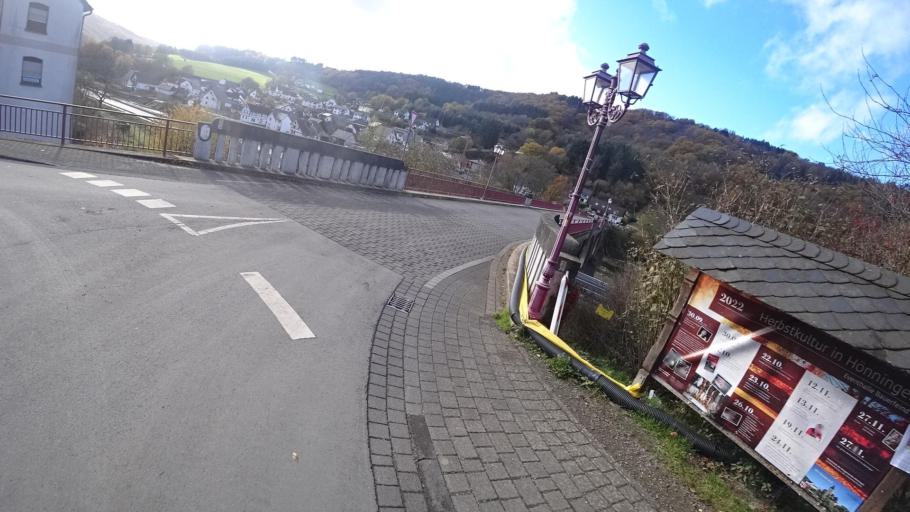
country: DE
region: Rheinland-Pfalz
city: Honningen
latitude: 50.4712
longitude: 6.9502
